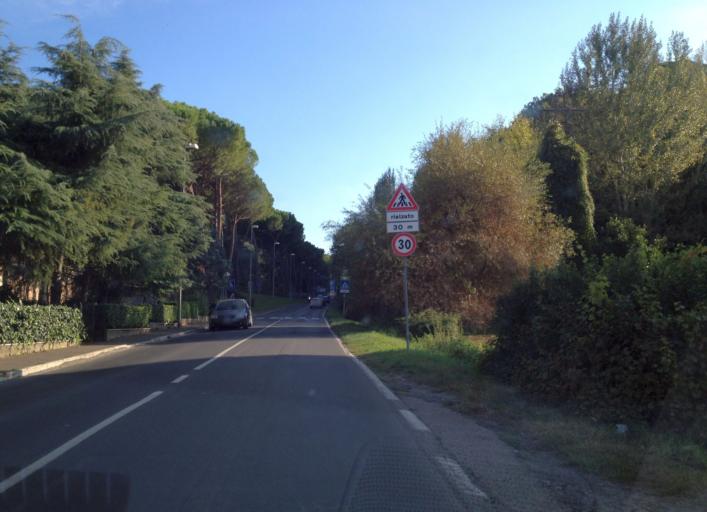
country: IT
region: Tuscany
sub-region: Provincia di Siena
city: Poggibonsi
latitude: 43.4656
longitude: 11.1447
